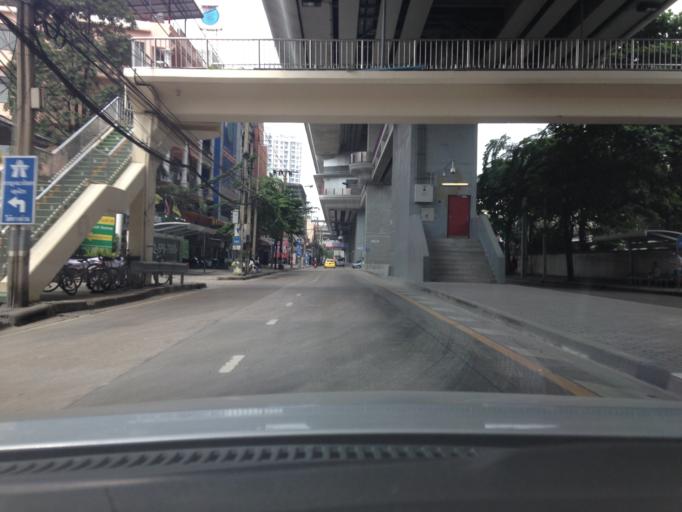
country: TH
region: Bangkok
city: Bang Sue
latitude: 13.8194
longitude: 100.5323
